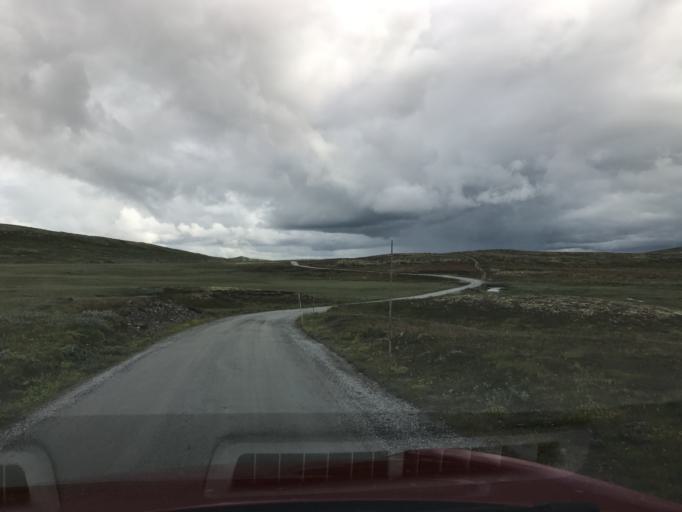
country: NO
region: Buskerud
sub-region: Hol
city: Geilo
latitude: 60.5509
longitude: 8.0752
